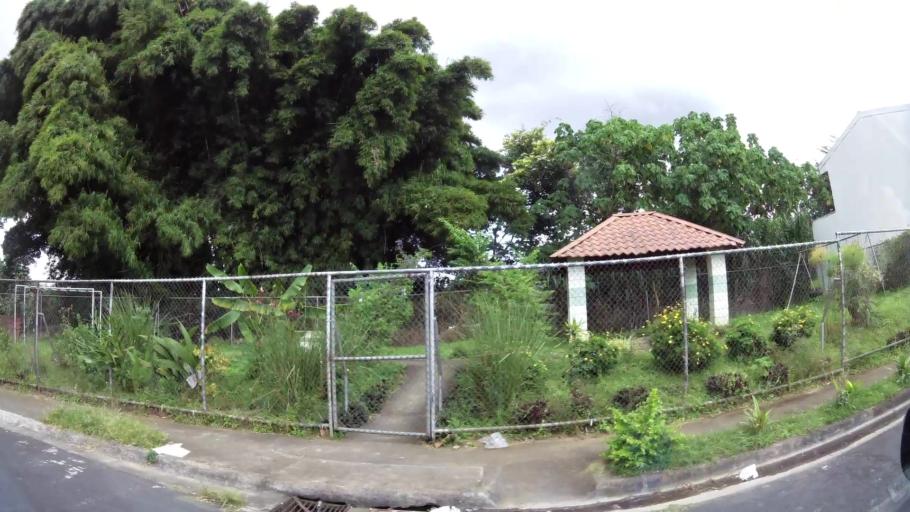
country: CR
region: Cartago
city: Concepcion
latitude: 9.9258
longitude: -84.0025
